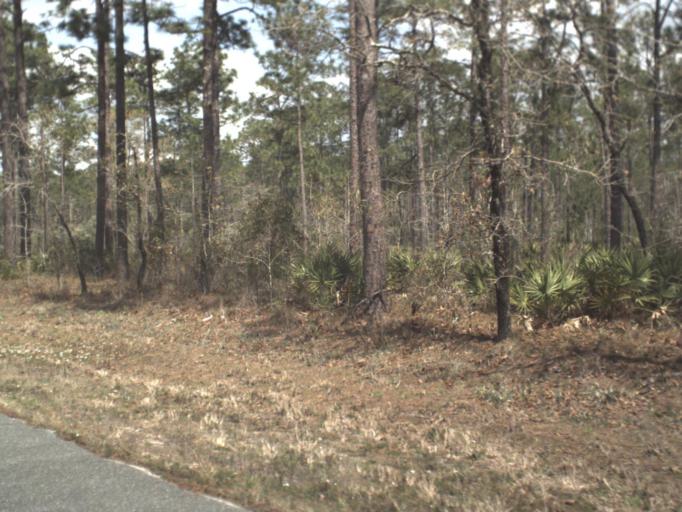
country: US
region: Florida
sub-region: Gulf County
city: Wewahitchka
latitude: 29.9872
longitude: -84.9761
